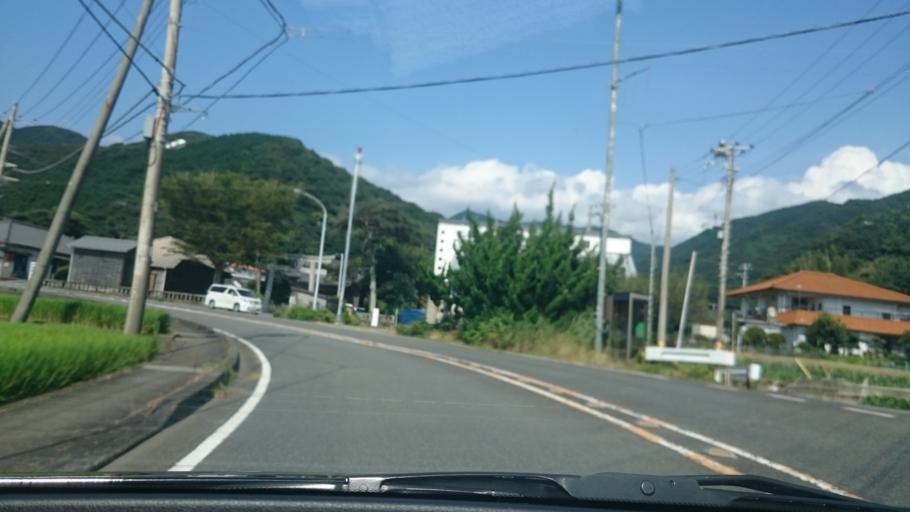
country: JP
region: Shizuoka
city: Heda
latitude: 34.9216
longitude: 138.7895
